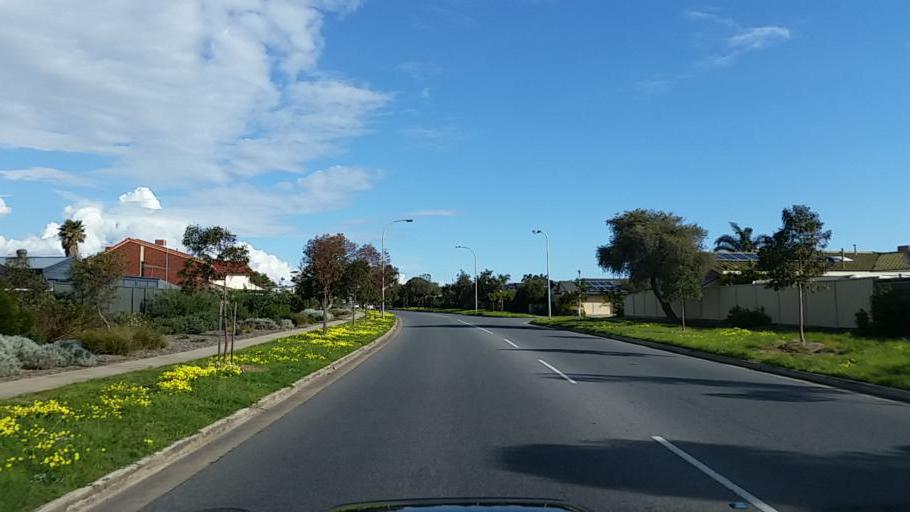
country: AU
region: South Australia
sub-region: Charles Sturt
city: West Lakes Shore
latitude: -34.8676
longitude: 138.4838
